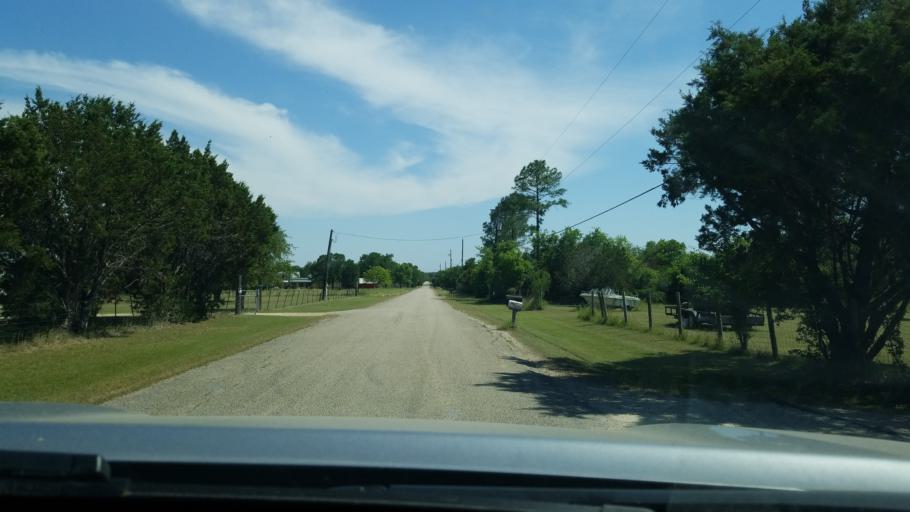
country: US
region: Texas
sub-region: Bexar County
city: Timberwood Park
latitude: 29.7552
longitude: -98.5179
